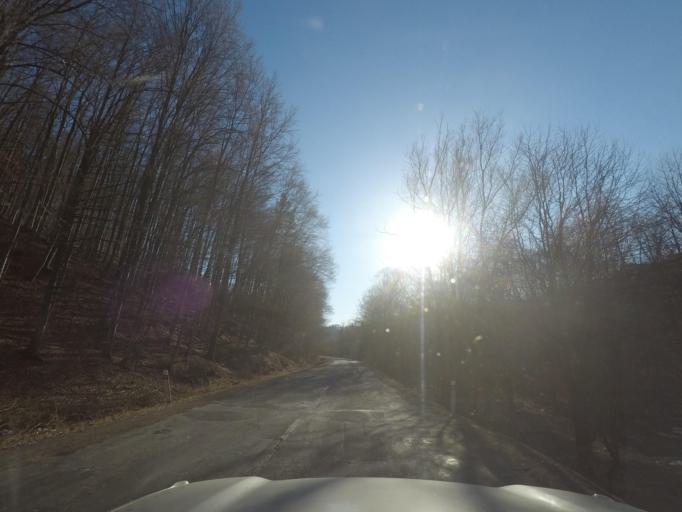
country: SK
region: Presovsky
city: Medzilaborce
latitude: 49.2786
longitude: 21.8121
